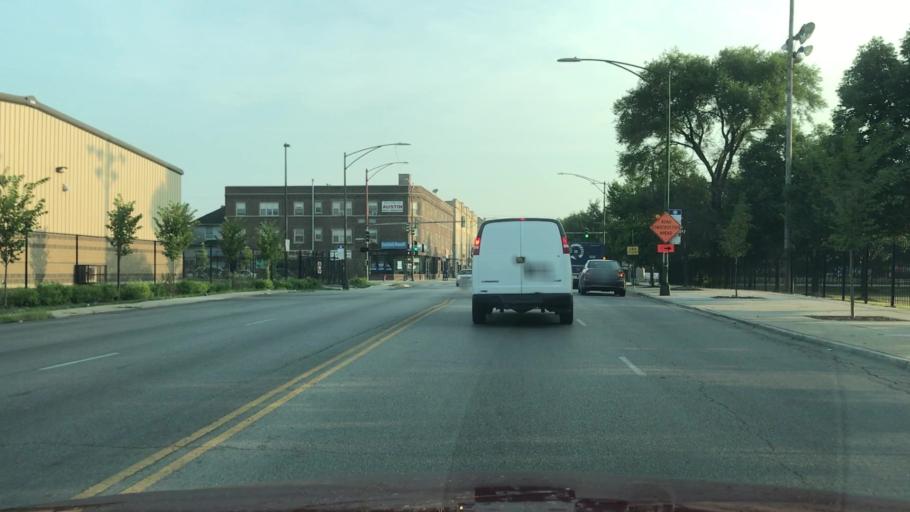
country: US
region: Illinois
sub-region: Cook County
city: Cicero
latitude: 41.8721
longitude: -87.7547
